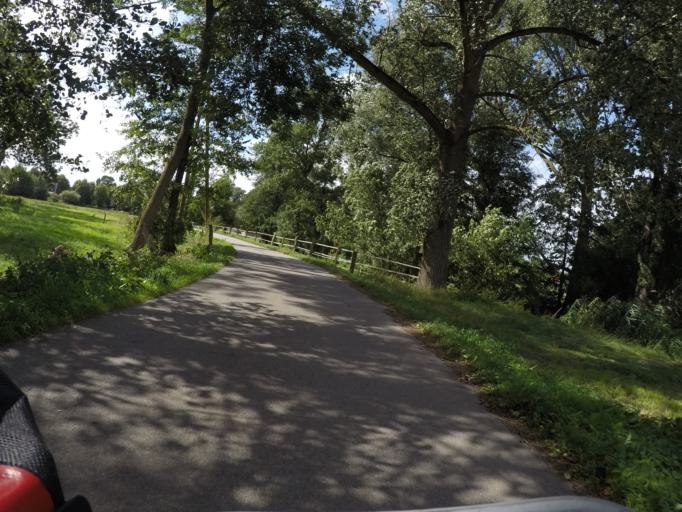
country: DE
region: Lower Saxony
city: Radbruch
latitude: 53.3646
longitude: 10.2921
